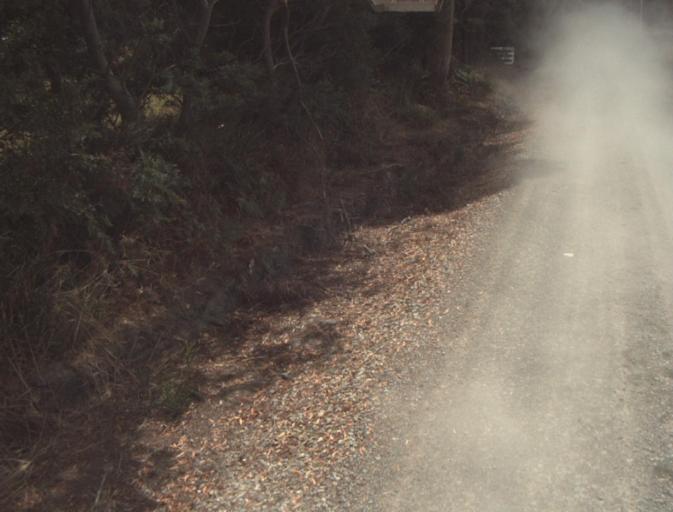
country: AU
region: Tasmania
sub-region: Launceston
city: Mayfield
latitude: -41.2397
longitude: 147.1620
